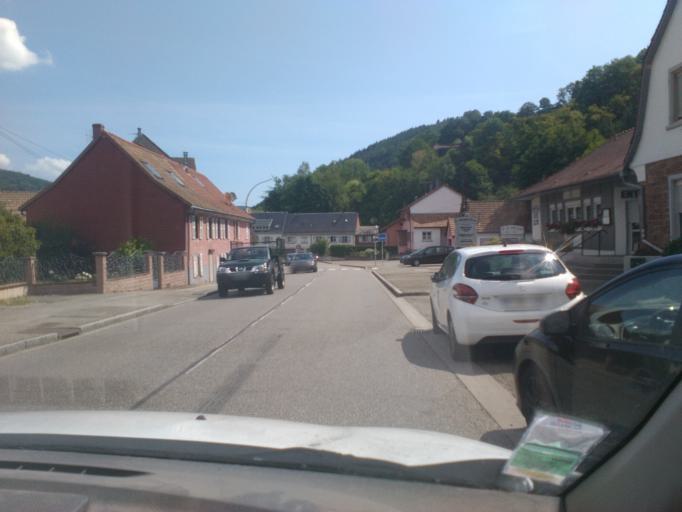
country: FR
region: Alsace
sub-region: Departement du Haut-Rhin
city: Lapoutroie
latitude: 48.1464
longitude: 7.1868
